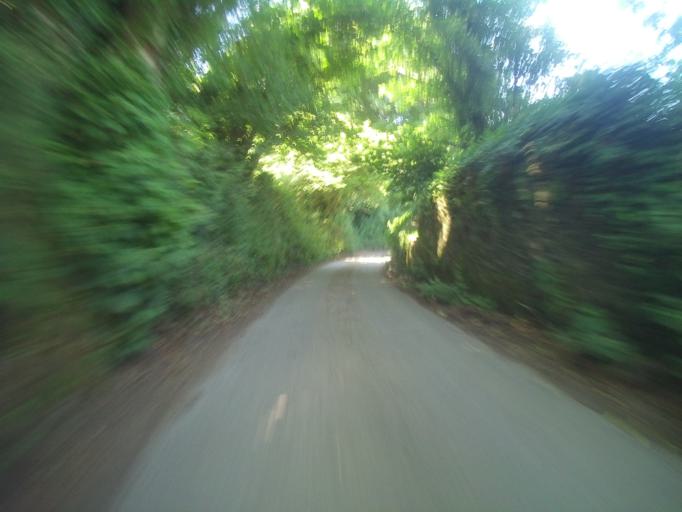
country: GB
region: England
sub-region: Devon
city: Dartmouth
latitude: 50.3540
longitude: -3.5977
